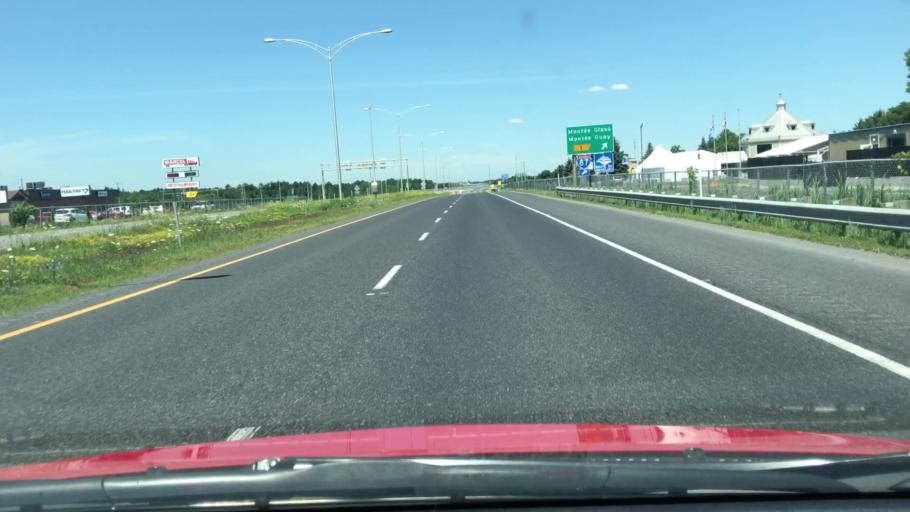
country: US
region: New York
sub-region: Clinton County
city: Champlain
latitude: 45.0148
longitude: -73.4526
